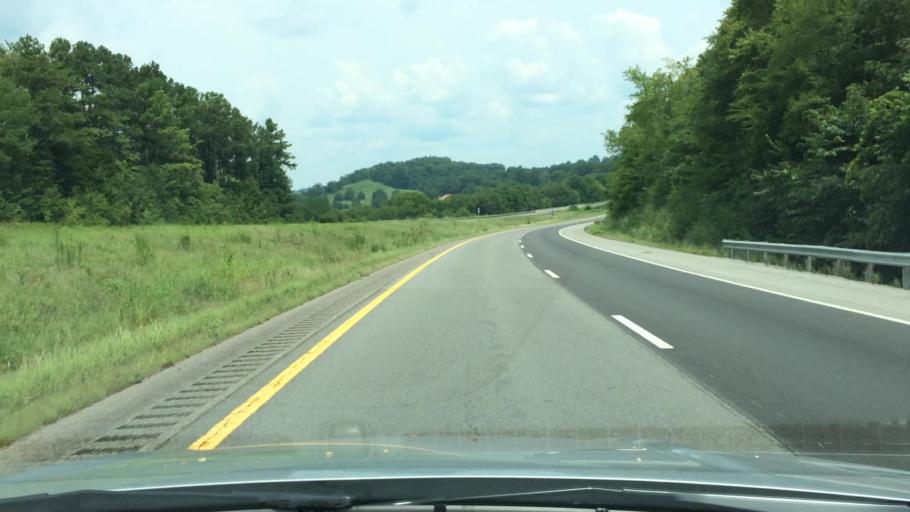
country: US
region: Tennessee
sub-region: Marshall County
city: Cornersville
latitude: 35.2686
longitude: -86.8896
